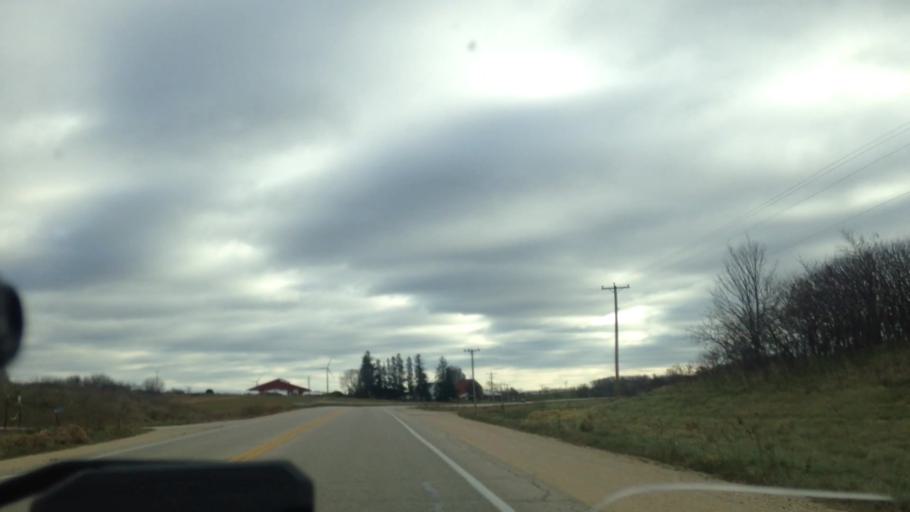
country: US
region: Wisconsin
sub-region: Dodge County
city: Mayville
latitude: 43.4433
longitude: -88.4960
